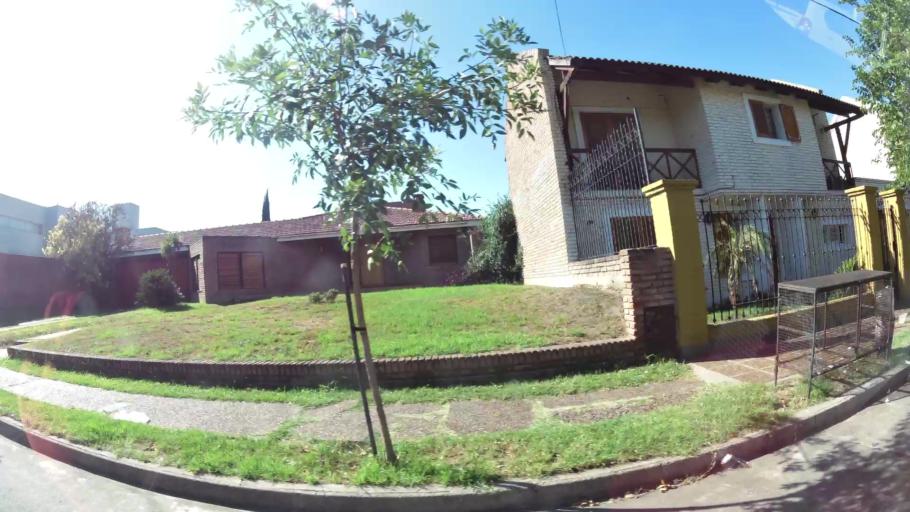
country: AR
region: Cordoba
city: Villa Allende
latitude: -31.3506
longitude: -64.2467
